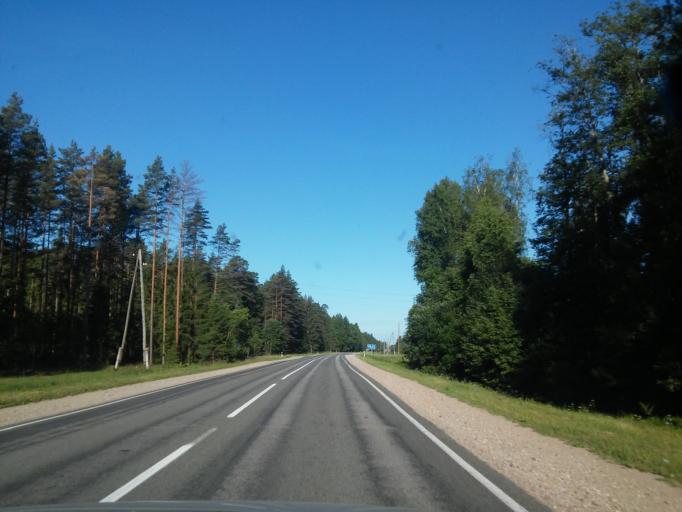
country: LV
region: Skrunda
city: Skrunda
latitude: 56.6790
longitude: 22.0734
